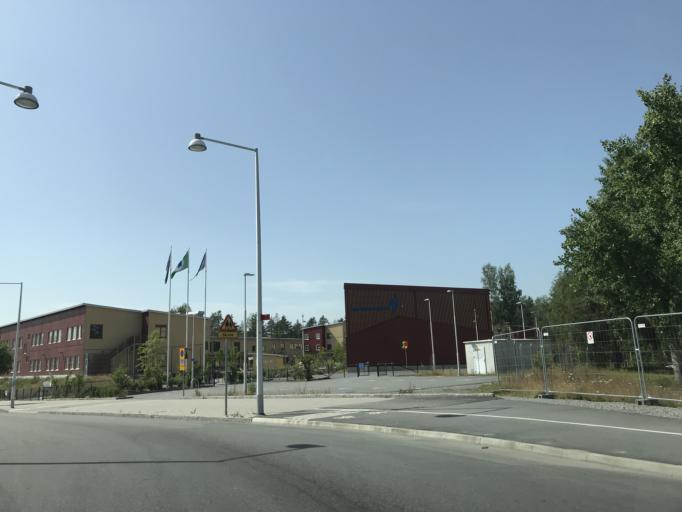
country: SE
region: Stockholm
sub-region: Solna Kommun
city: Rasunda
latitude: 59.3837
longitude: 17.9894
